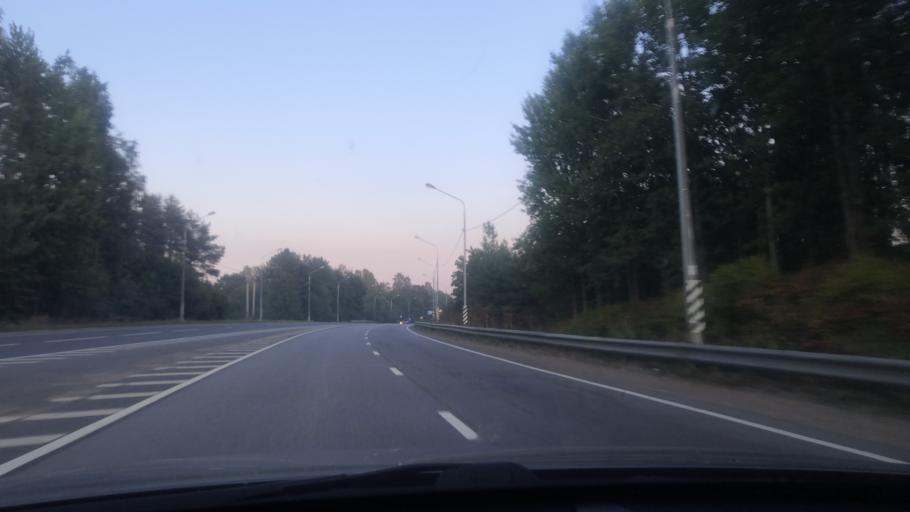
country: RU
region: St.-Petersburg
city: Beloostrov
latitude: 60.1980
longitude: 30.0254
